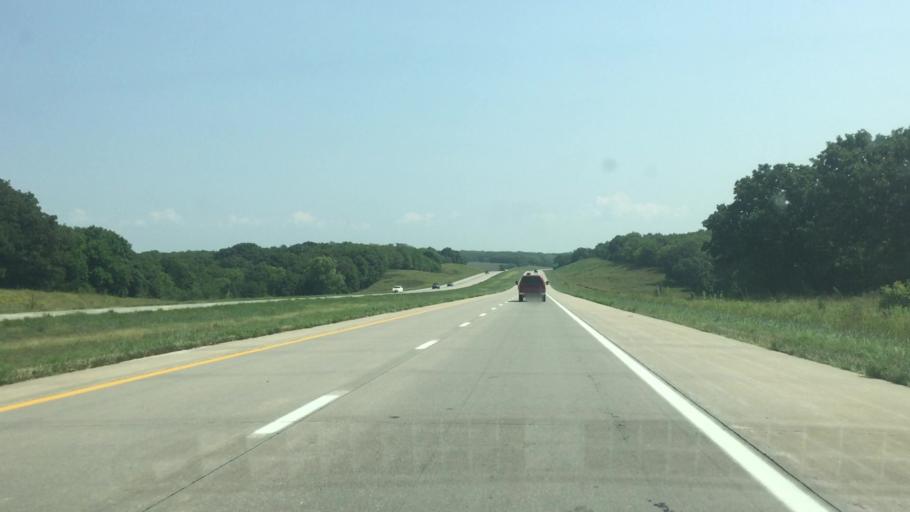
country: US
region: Kansas
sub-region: Osage County
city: Lyndon
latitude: 38.4785
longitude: -95.5035
